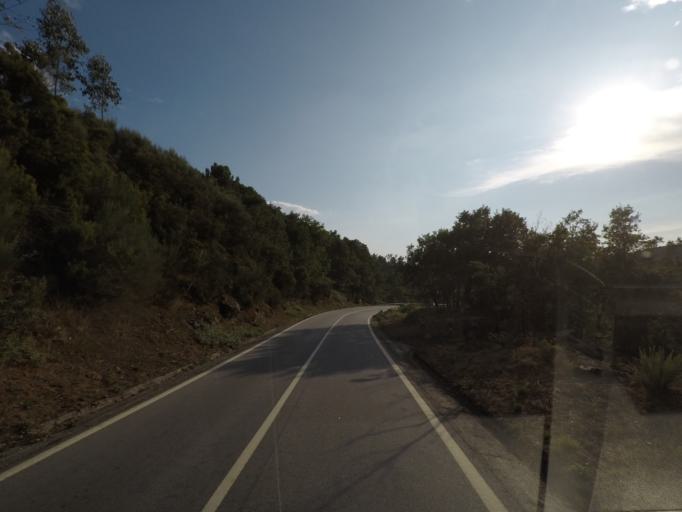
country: PT
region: Porto
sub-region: Baiao
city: Valadares
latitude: 41.2028
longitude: -7.9647
